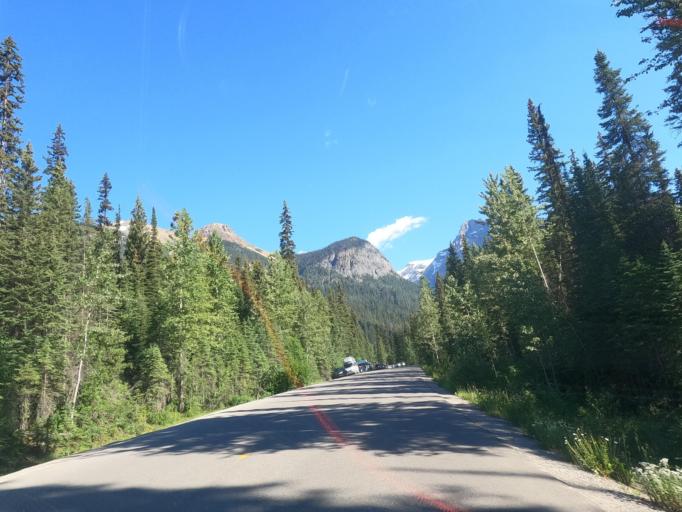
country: CA
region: Alberta
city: Lake Louise
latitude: 51.4364
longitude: -116.5400
